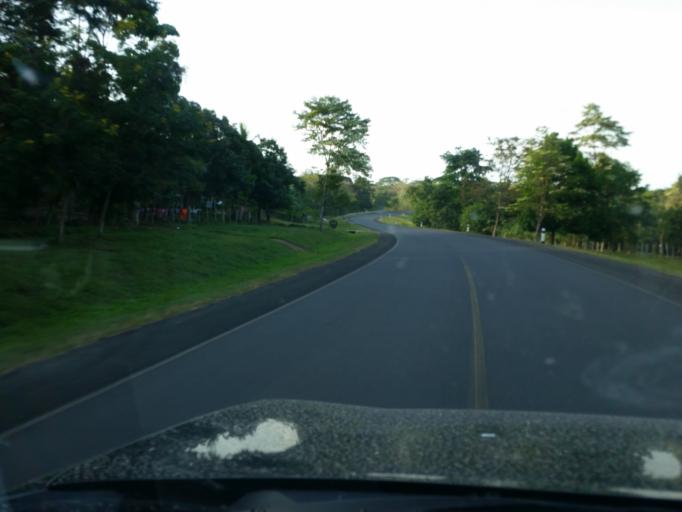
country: NI
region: Rio San Juan
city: San Carlos
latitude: 11.2610
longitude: -84.7121
